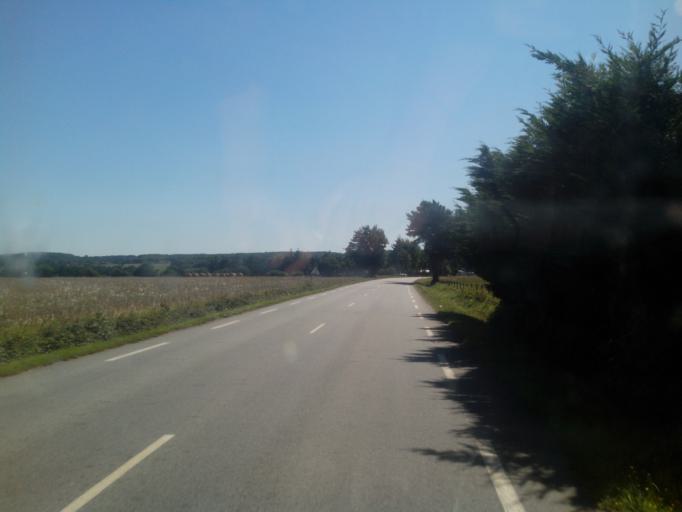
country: FR
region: Brittany
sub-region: Departement du Morbihan
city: Guegon
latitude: 47.9210
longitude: -2.5268
